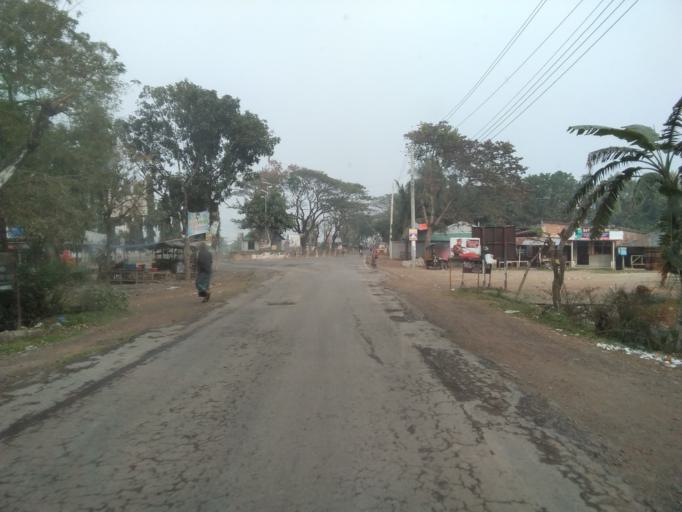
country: BD
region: Khulna
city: Satkhira
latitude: 22.6883
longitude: 89.0324
